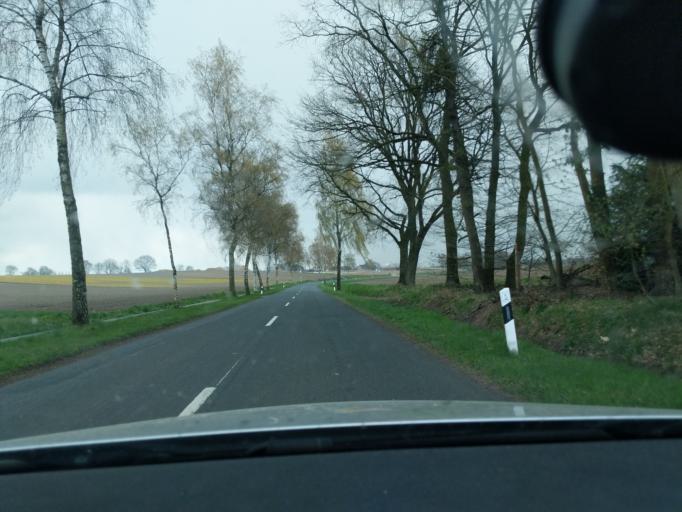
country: DE
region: Lower Saxony
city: Horneburg
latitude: 53.5103
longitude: 9.5527
